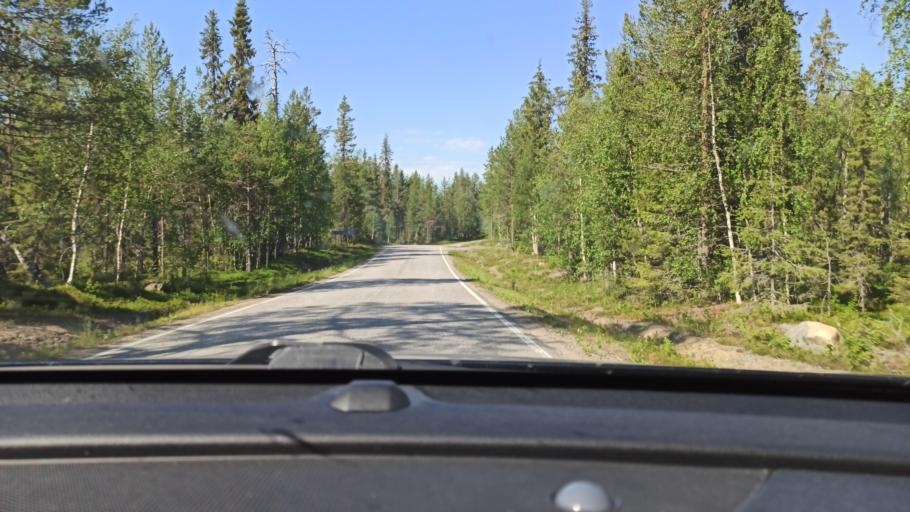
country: FI
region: Lapland
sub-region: Tunturi-Lappi
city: Kolari
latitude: 67.6842
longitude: 24.1079
